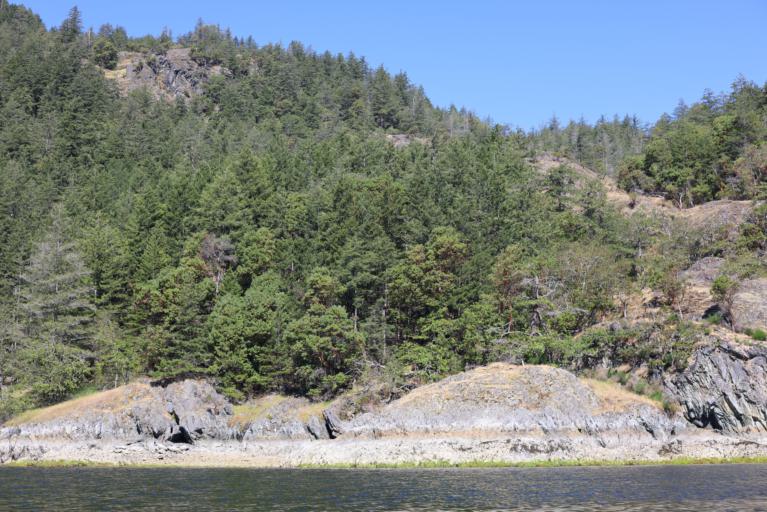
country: CA
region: British Columbia
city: North Cowichan
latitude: 48.8370
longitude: -123.5884
